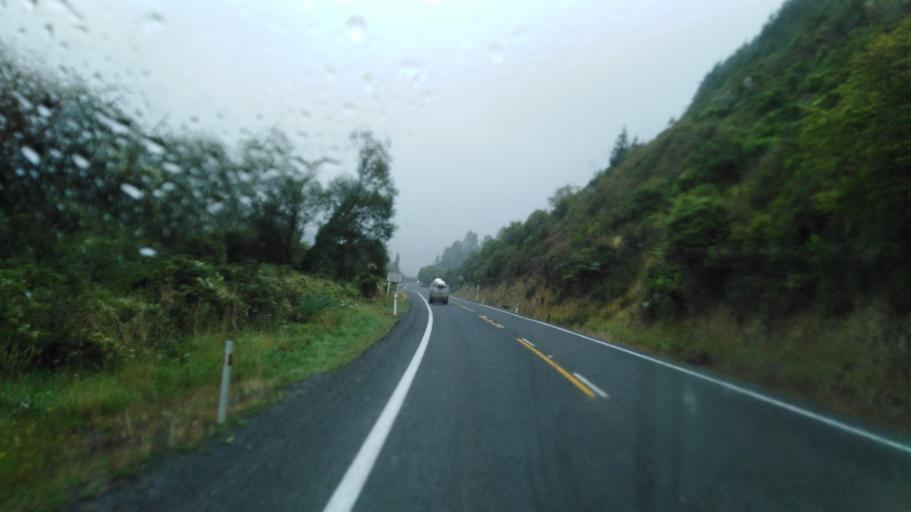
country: NZ
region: Marlborough
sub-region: Marlborough District
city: Picton
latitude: -41.3852
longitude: 173.9516
